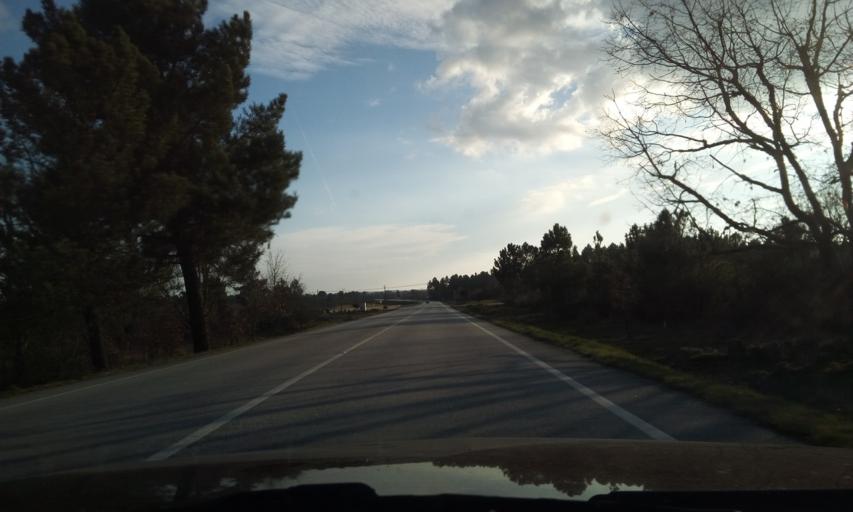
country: PT
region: Guarda
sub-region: Pinhel
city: Pinhel
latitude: 40.6406
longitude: -6.9704
